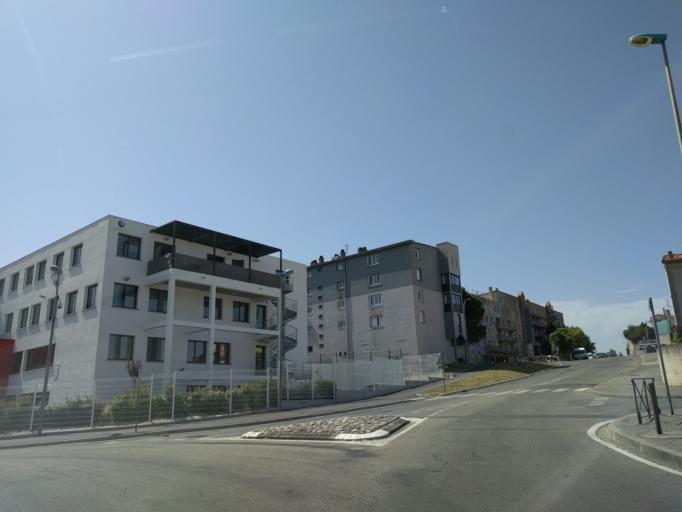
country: FR
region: Languedoc-Roussillon
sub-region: Departement de l'Aude
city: Carcassonne
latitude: 43.2151
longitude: 2.3669
